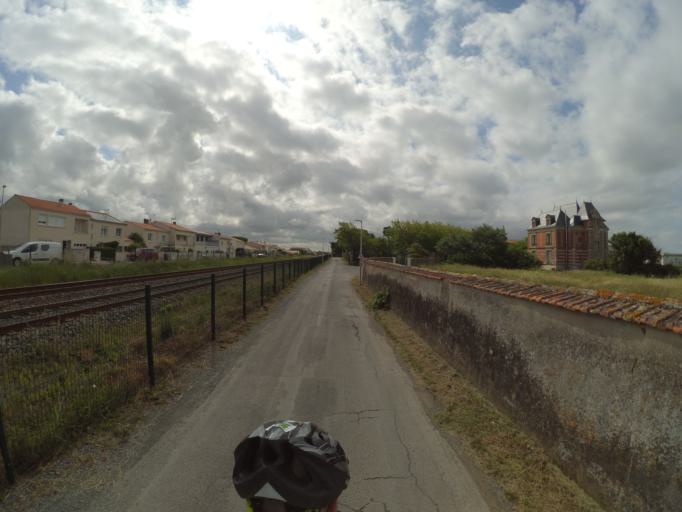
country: FR
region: Poitou-Charentes
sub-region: Departement de la Charente-Maritime
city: Angoulins
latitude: 46.0973
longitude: -1.1045
